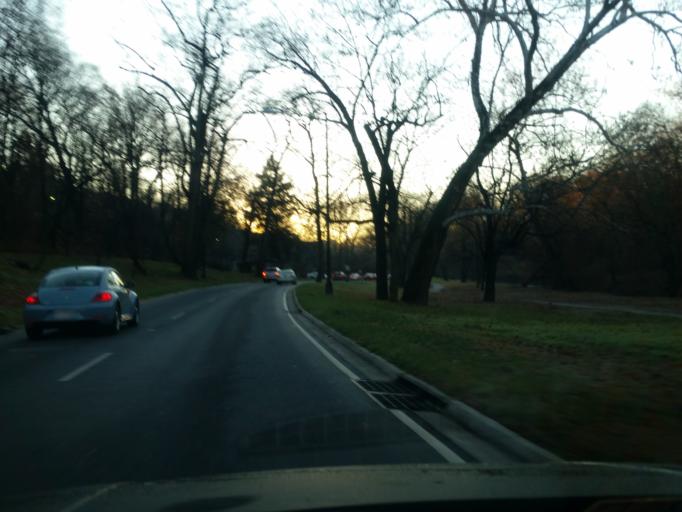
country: US
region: Washington, D.C.
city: Washington, D.C.
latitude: 38.9147
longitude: -77.0569
